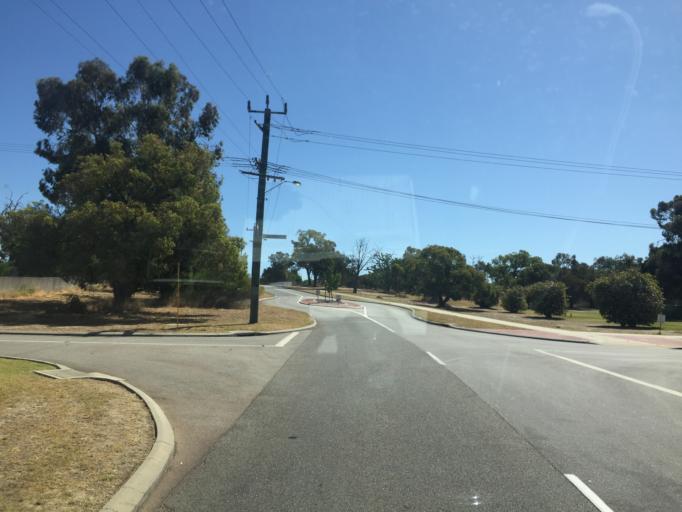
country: AU
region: Western Australia
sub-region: Belmont
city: Redcliffe
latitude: -31.9356
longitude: 115.9467
